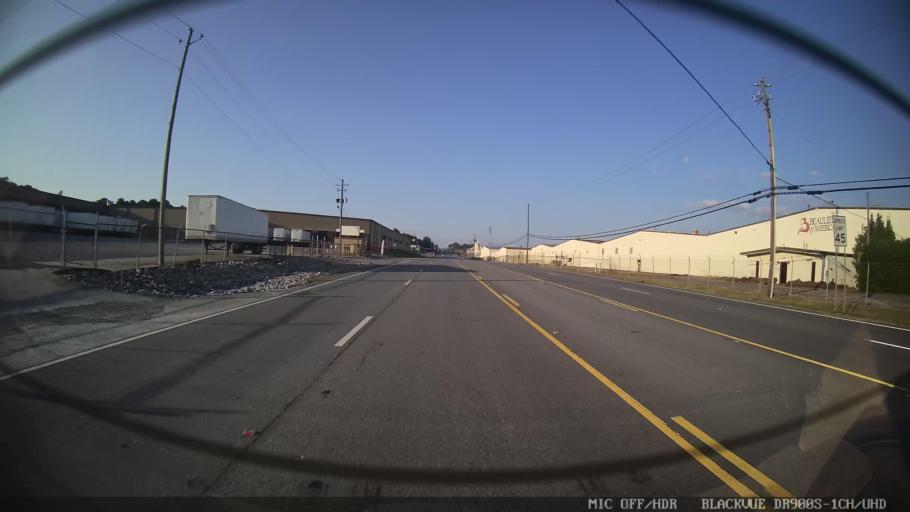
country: US
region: Georgia
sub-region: Murray County
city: Chatsworth
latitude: 34.8273
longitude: -84.7623
